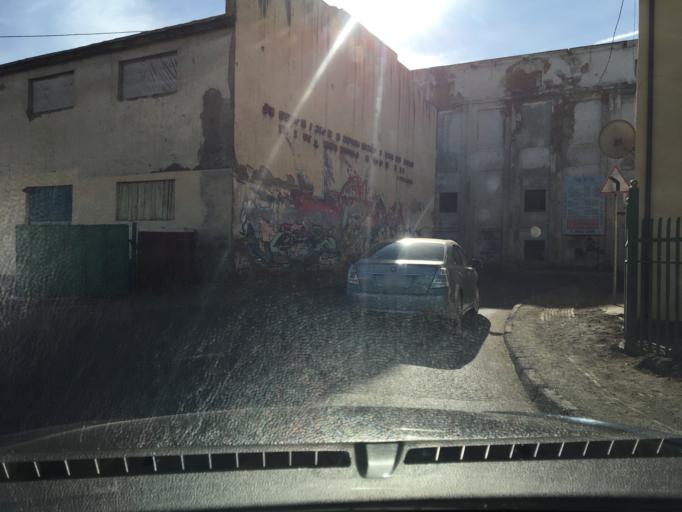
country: MN
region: Ulaanbaatar
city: Ulaanbaatar
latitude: 47.8945
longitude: 106.8961
